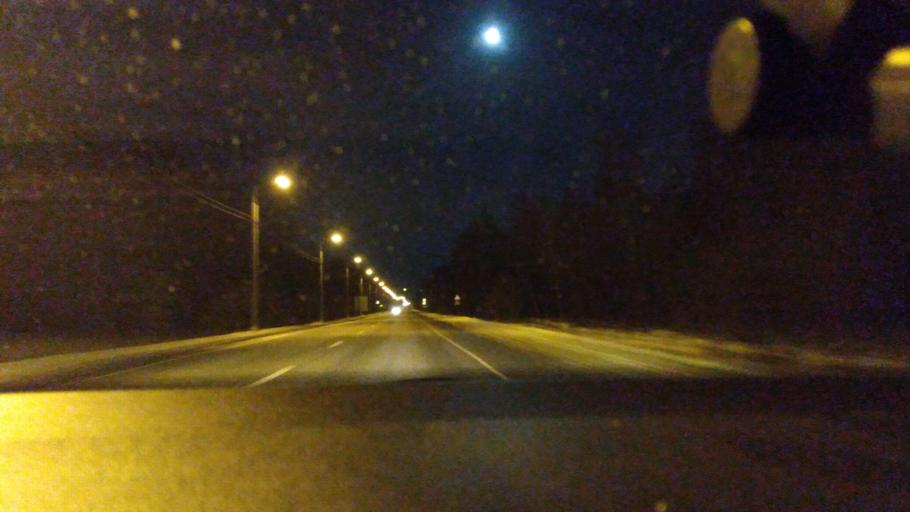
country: RU
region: Moskovskaya
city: Il'inskiy Pogost
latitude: 55.4884
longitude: 38.8888
